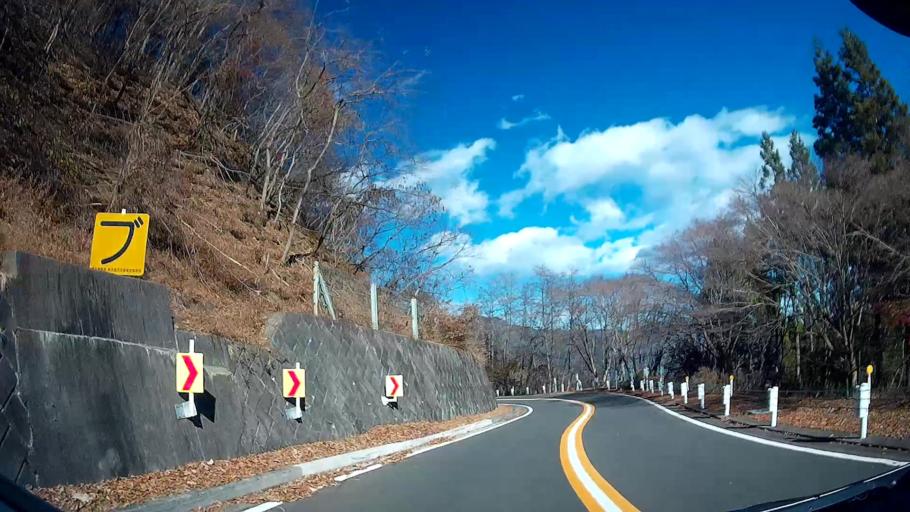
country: JP
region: Yamanashi
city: Uenohara
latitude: 35.7623
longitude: 139.0383
